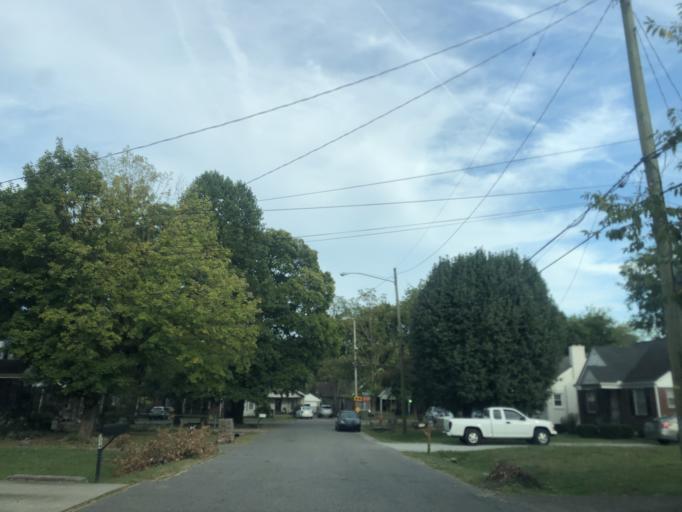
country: US
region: Tennessee
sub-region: Davidson County
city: Oak Hill
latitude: 36.1023
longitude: -86.7357
